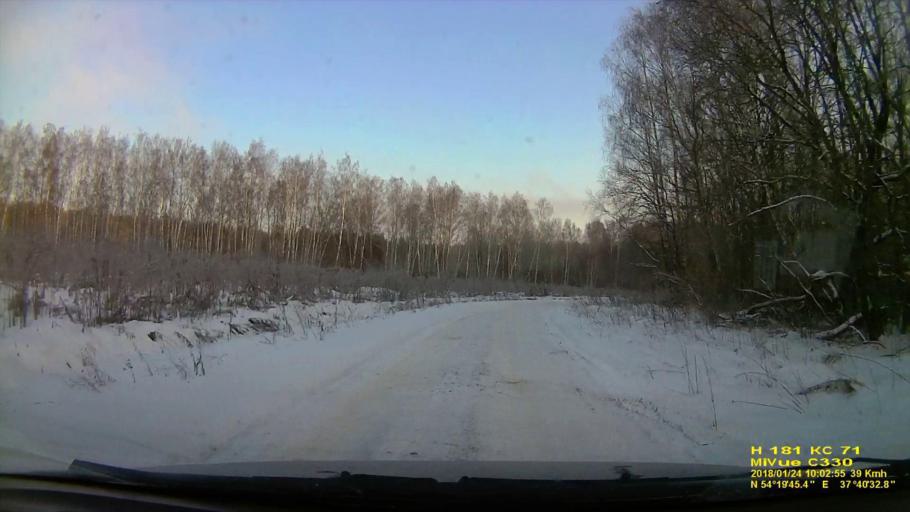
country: RU
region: Tula
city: Revyakino
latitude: 54.3293
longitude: 37.6759
